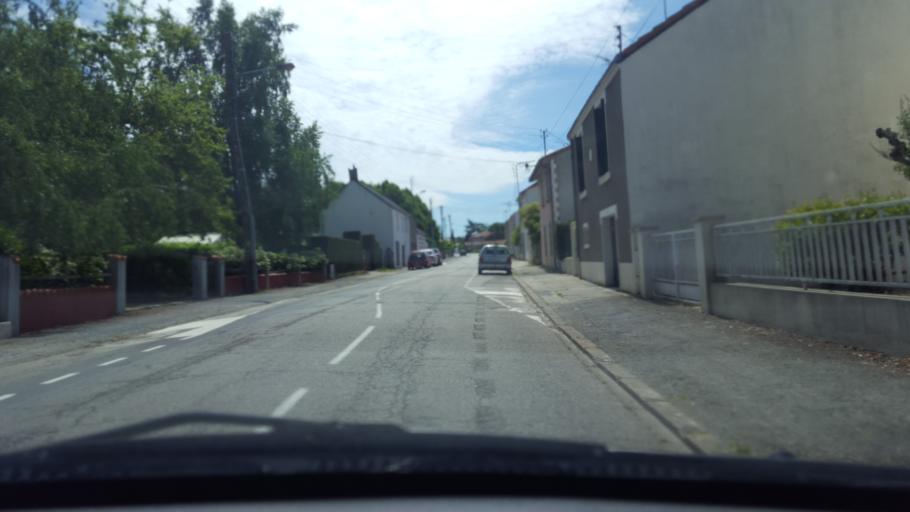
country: FR
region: Pays de la Loire
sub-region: Departement de la Loire-Atlantique
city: Saint-Philbert-de-Grand-Lieu
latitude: 47.0334
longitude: -1.6424
